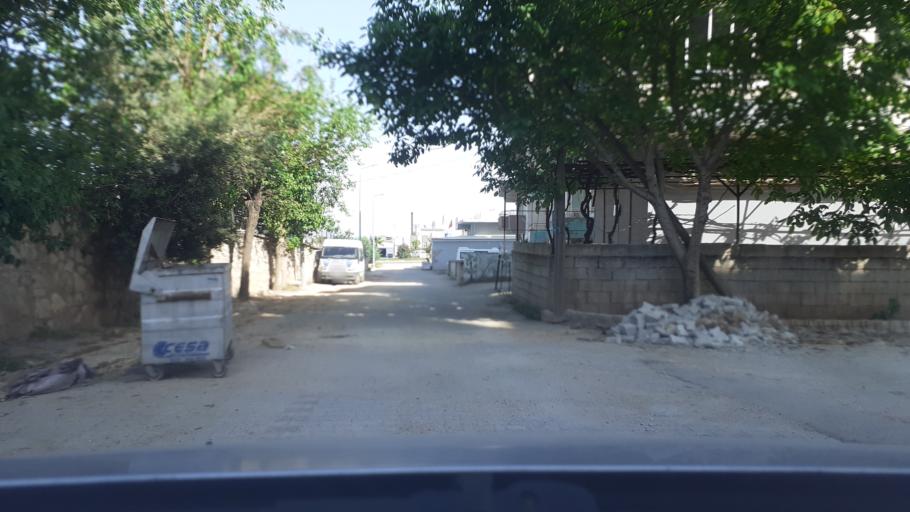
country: TR
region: Hatay
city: Kirikhan
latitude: 36.4919
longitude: 36.3686
